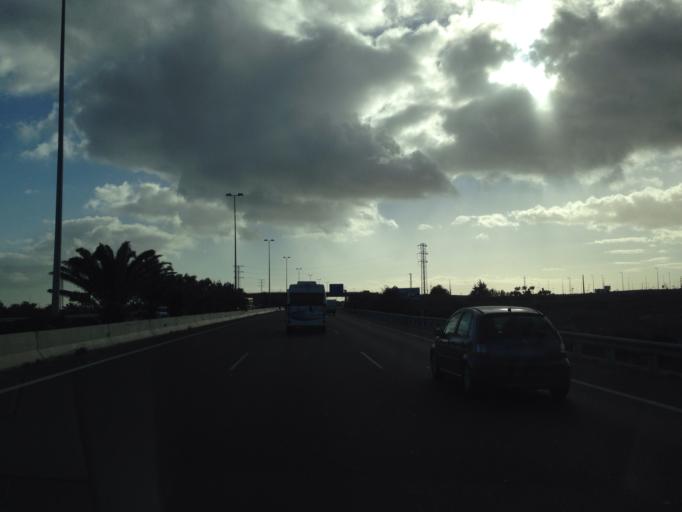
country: ES
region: Canary Islands
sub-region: Provincia de Las Palmas
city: Cruce de Arinaga
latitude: 27.8342
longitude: -15.4432
